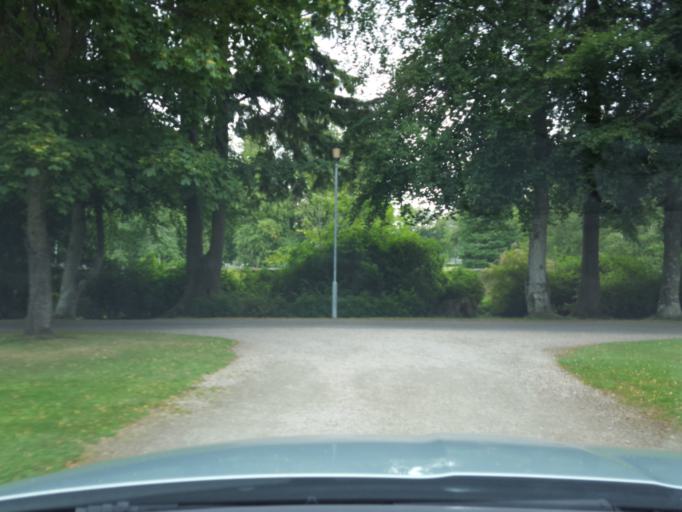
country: GB
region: Scotland
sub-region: Aberdeenshire
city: Alford
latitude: 57.2411
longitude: -2.6959
